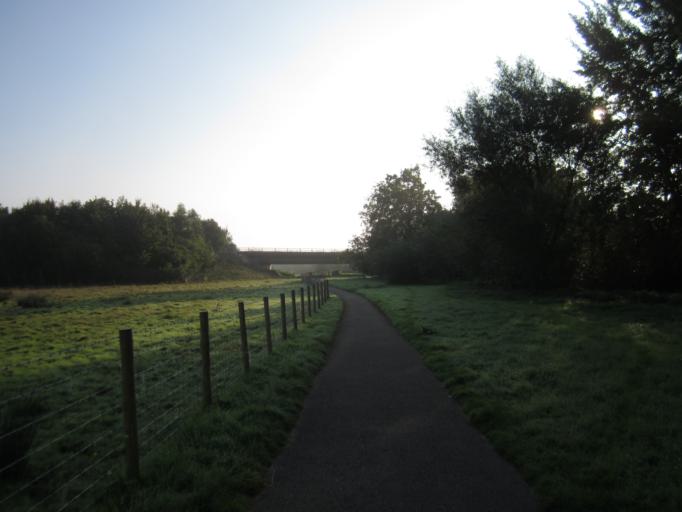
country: GB
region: England
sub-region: Kent
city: Canterbury
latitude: 51.2719
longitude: 1.0554
